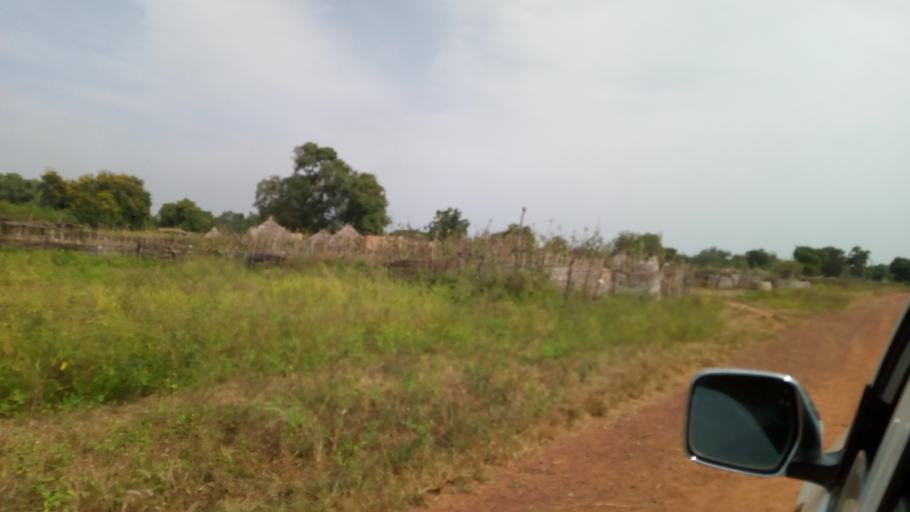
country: ML
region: Kayes
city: Kita
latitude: 13.2615
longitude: -8.8554
